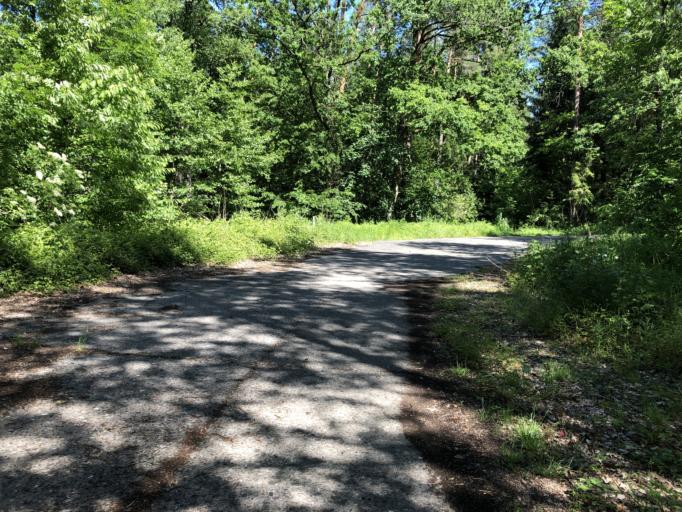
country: DE
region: Bavaria
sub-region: Upper Franconia
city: Memmelsdorf
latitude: 49.9193
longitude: 10.9610
